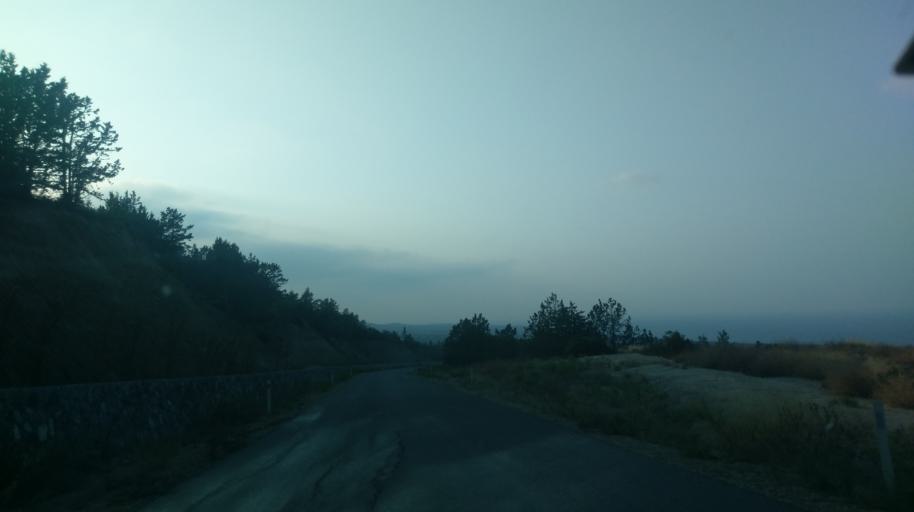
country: CY
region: Ammochostos
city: Trikomo
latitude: 35.4023
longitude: 33.8583
